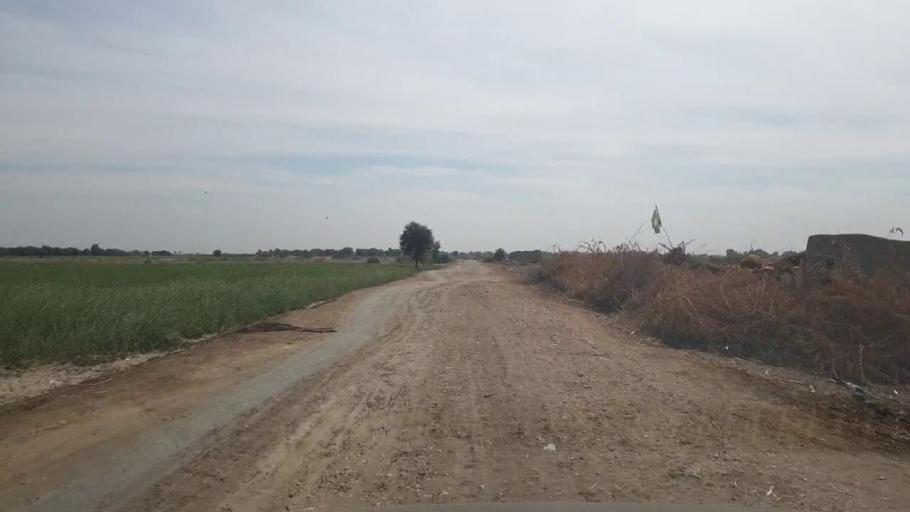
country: PK
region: Sindh
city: Kunri
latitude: 25.3005
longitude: 69.5766
